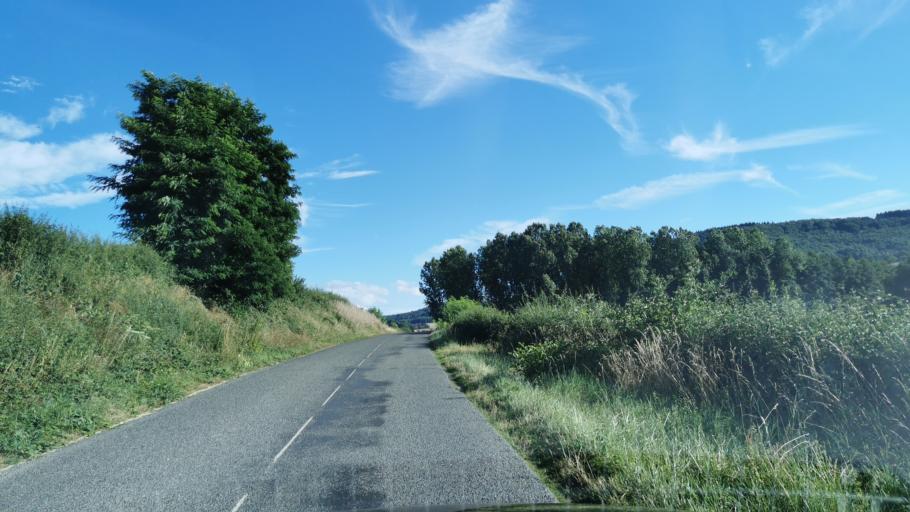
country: FR
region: Bourgogne
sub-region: Departement de Saone-et-Loire
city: Marmagne
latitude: 46.8452
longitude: 4.3194
